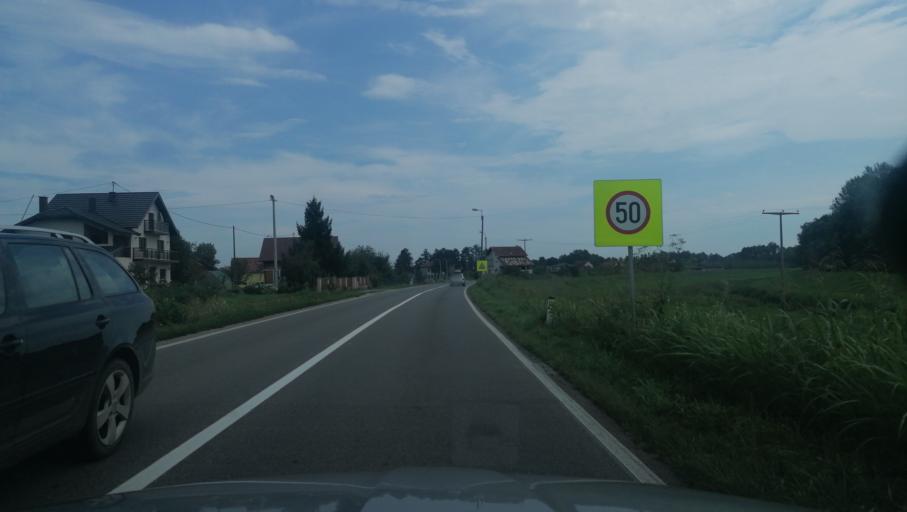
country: BA
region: Brcko
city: Brka
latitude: 44.9287
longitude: 18.7128
